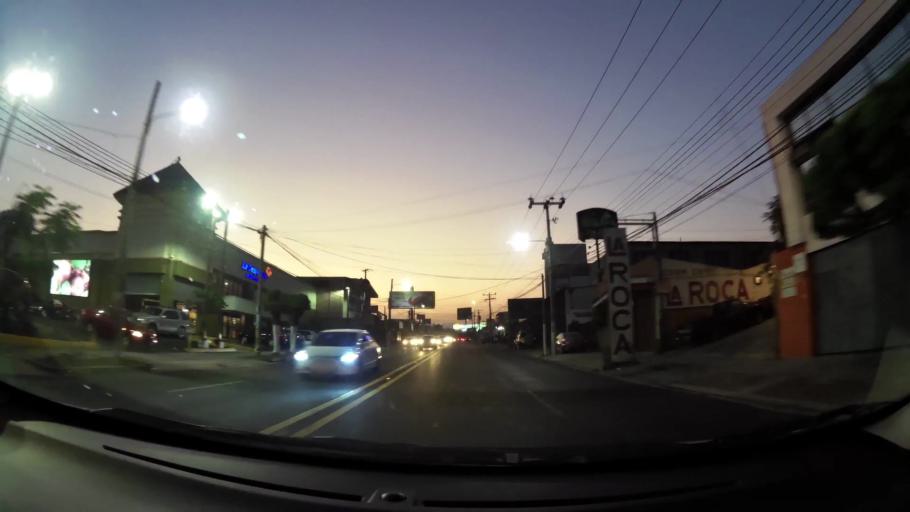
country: SV
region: La Libertad
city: Santa Tecla
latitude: 13.6781
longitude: -89.2655
